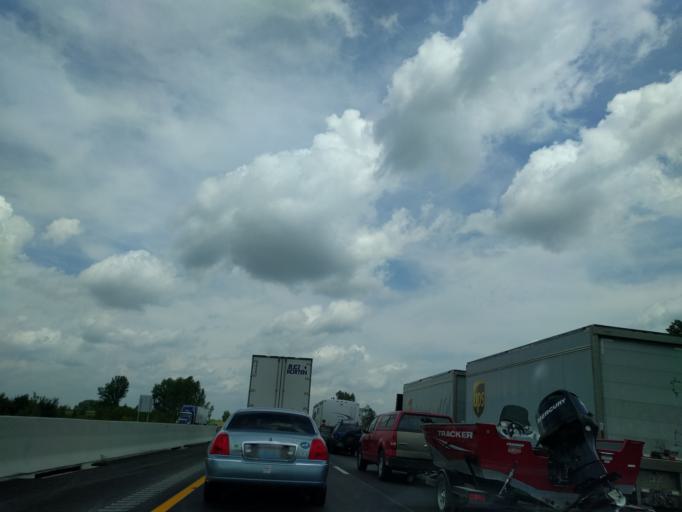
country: US
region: Kentucky
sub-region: Larue County
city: Hodgenville
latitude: 37.5325
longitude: -85.8824
